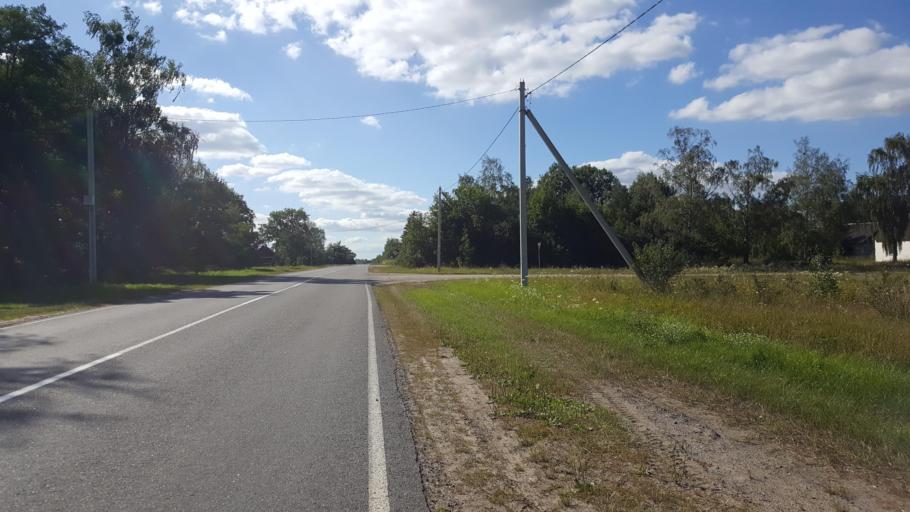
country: BY
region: Brest
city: Kobryn
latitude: 52.3530
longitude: 24.1875
